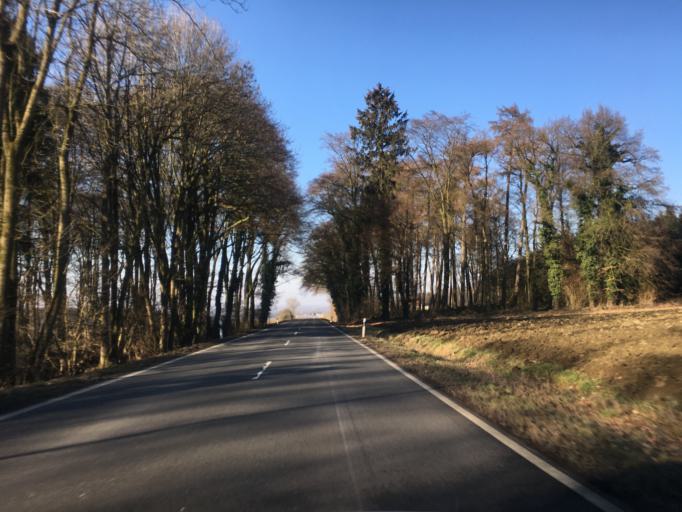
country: DE
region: North Rhine-Westphalia
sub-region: Regierungsbezirk Munster
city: Billerbeck
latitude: 52.0054
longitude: 7.2798
